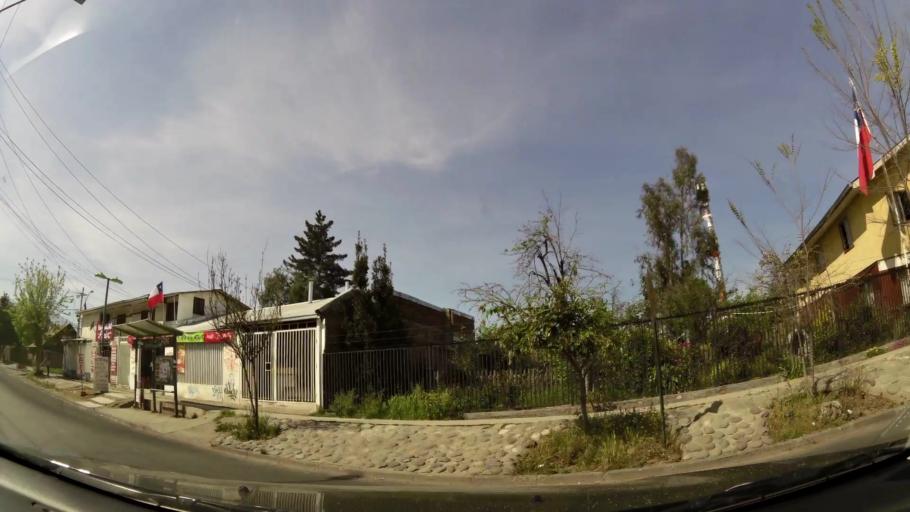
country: CL
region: Santiago Metropolitan
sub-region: Provincia de Cordillera
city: Puente Alto
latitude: -33.6233
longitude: -70.5849
